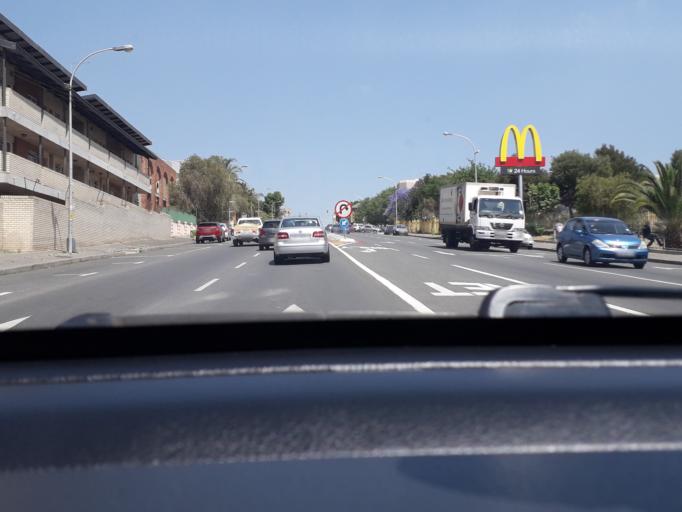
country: ZA
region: Gauteng
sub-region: City of Johannesburg Metropolitan Municipality
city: Modderfontein
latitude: -26.1388
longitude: 28.1516
